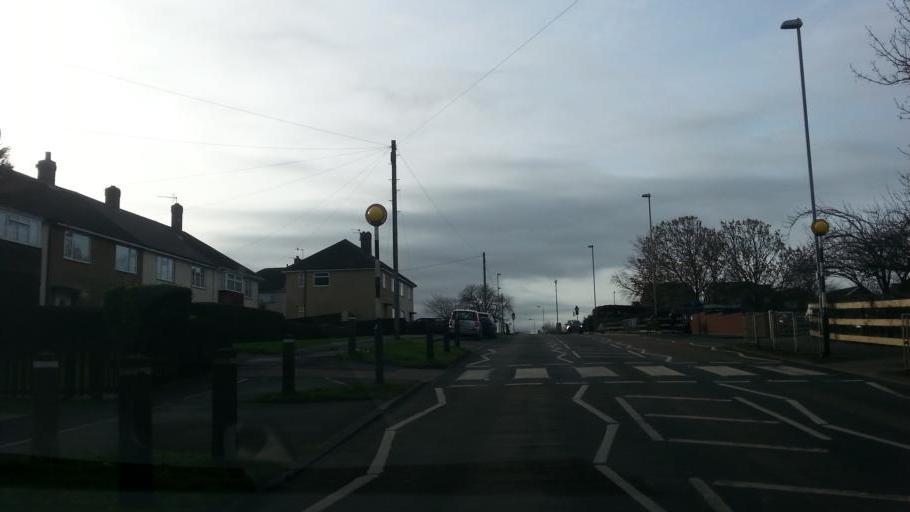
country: GB
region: England
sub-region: Leicestershire
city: Melton Mowbray
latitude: 52.7530
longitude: -0.8898
